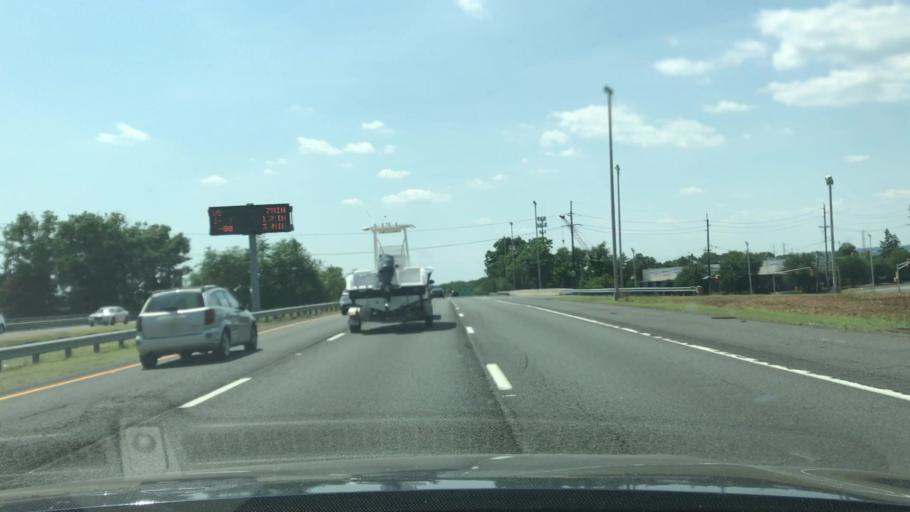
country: US
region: New Jersey
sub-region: Middlesex County
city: Society Hill
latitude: 40.5567
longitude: -74.4607
